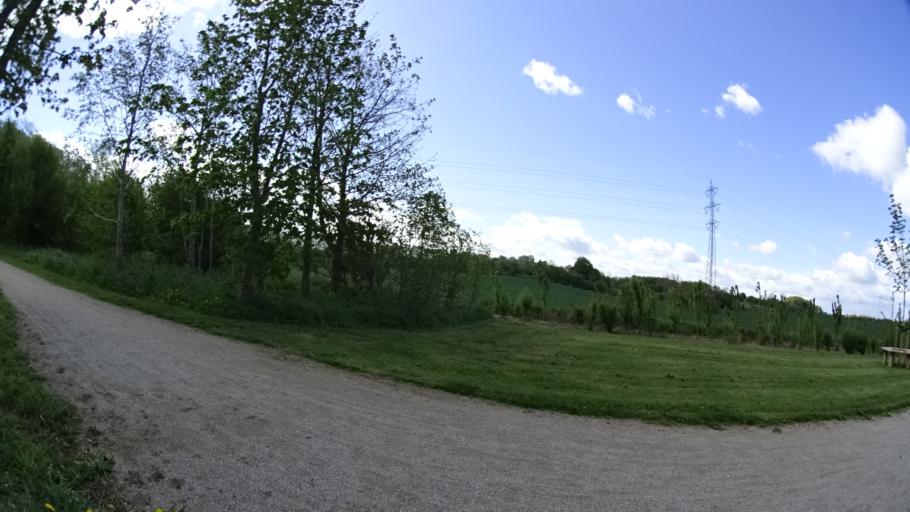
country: DK
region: Central Jutland
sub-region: Arhus Kommune
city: Stavtrup
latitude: 56.1261
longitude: 10.1052
